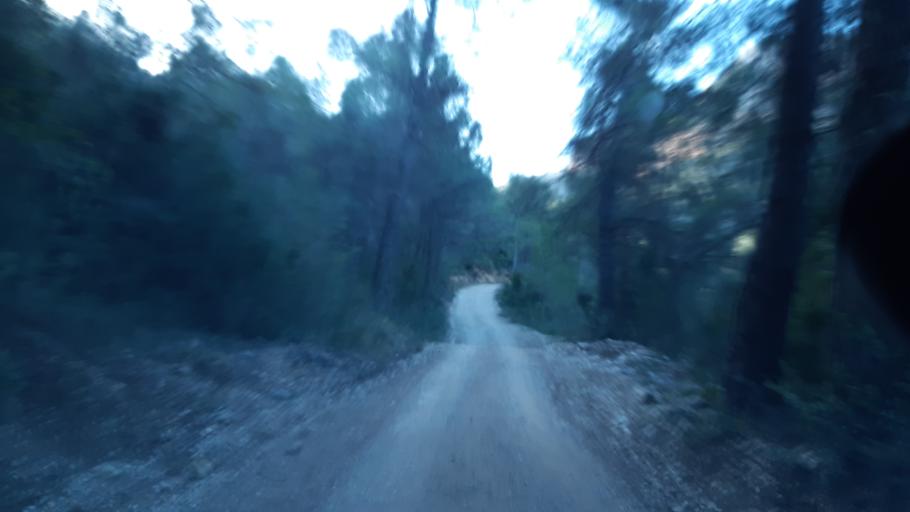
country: ES
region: Aragon
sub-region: Provincia de Teruel
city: Lledo
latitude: 40.8588
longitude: 0.2534
